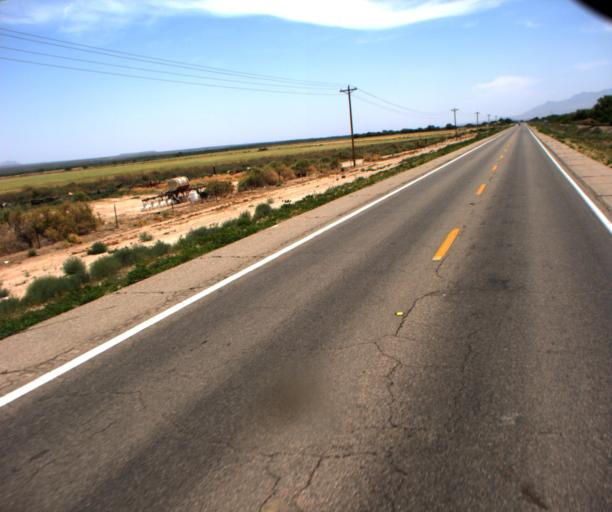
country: US
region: Arizona
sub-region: Graham County
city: Pima
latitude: 33.0192
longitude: -109.9542
